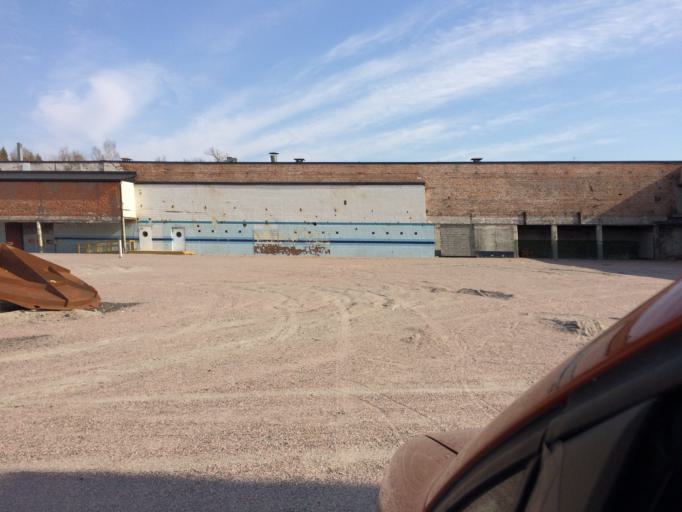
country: SE
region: Soedermanland
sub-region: Flens Kommun
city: Halleforsnas
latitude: 59.1519
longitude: 16.4882
